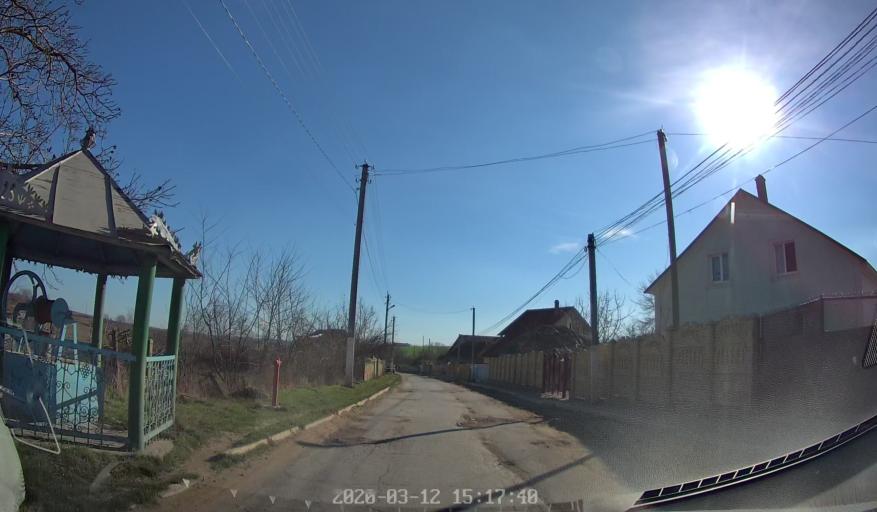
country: MD
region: Chisinau
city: Ciorescu
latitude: 47.2197
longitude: 28.9347
